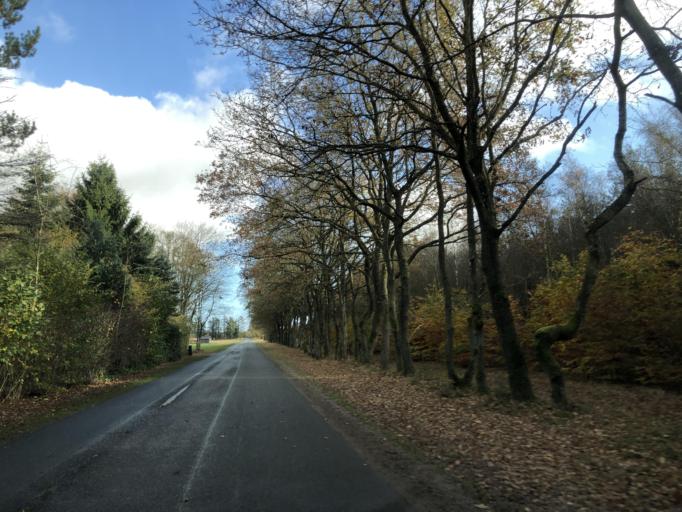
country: DK
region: Central Jutland
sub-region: Ringkobing-Skjern Kommune
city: Ringkobing
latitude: 56.1379
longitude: 8.3365
